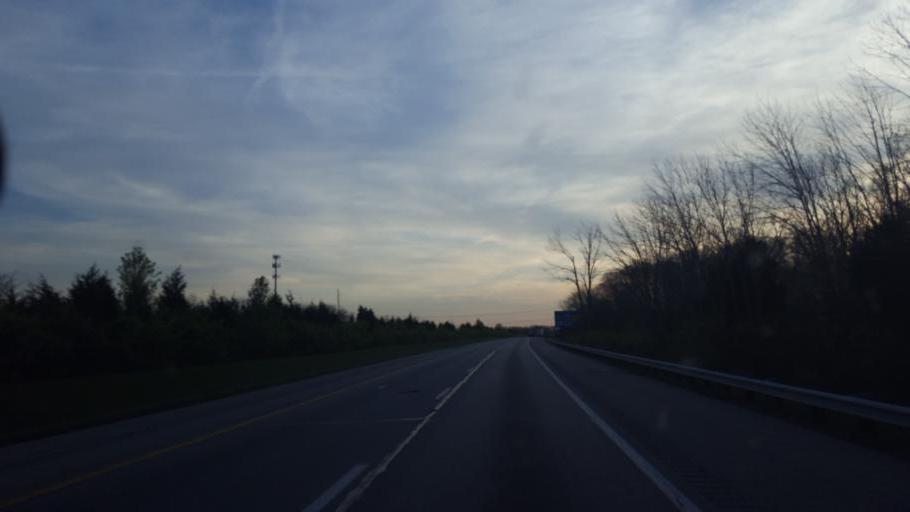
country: US
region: Ohio
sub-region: Warren County
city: South Lebanon
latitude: 39.3862
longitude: -84.2113
